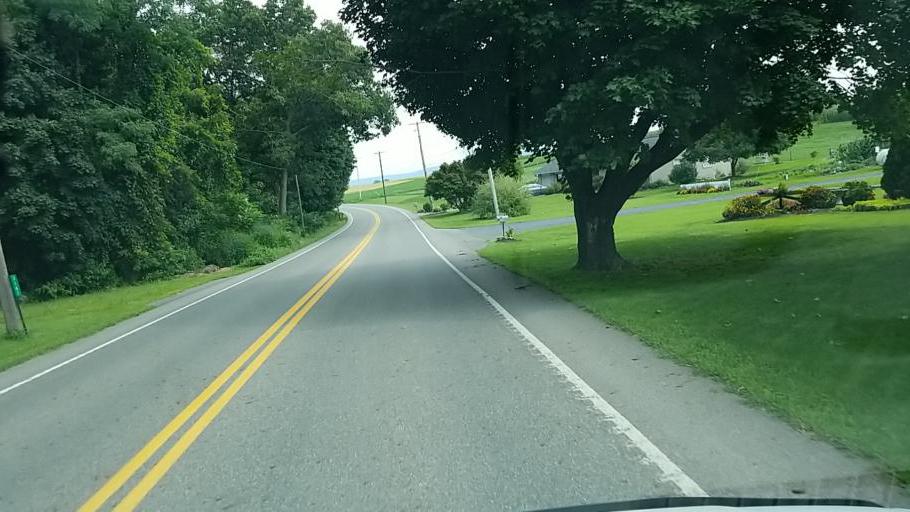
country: US
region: Pennsylvania
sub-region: Dauphin County
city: Elizabethville
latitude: 40.5842
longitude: -76.8567
